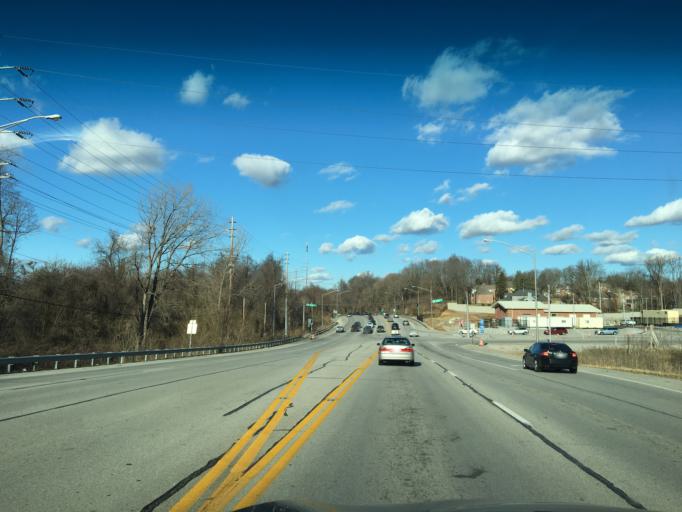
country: US
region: Kentucky
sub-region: Jefferson County
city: Prospect
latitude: 38.3223
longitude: -85.6222
